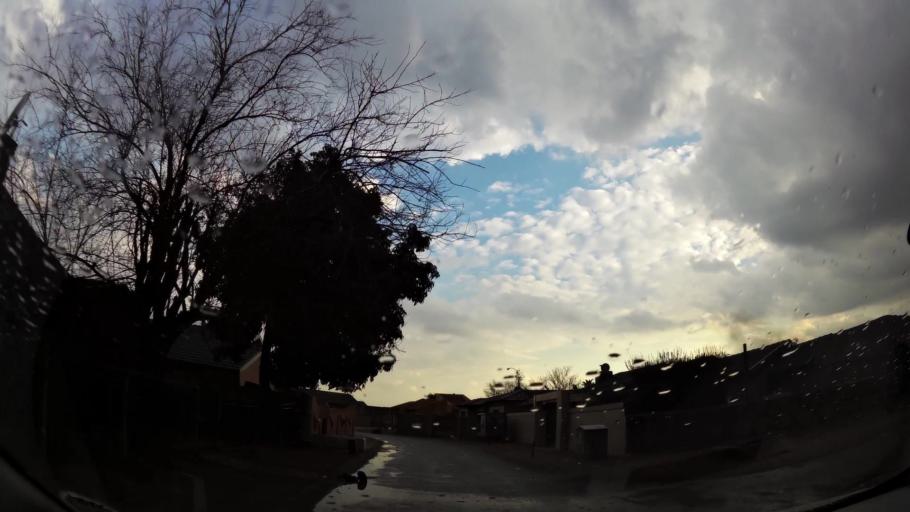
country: ZA
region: Gauteng
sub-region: Ekurhuleni Metropolitan Municipality
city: Germiston
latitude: -26.3541
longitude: 28.1294
